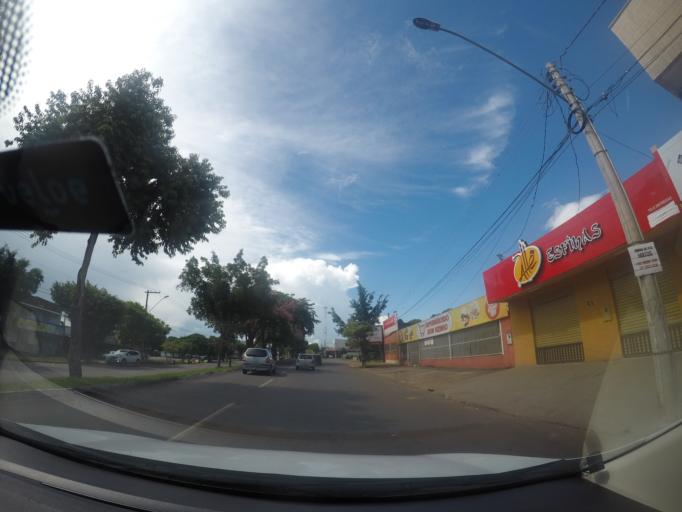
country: BR
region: Goias
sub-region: Trindade
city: Trindade
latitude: -16.6603
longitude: -49.3860
